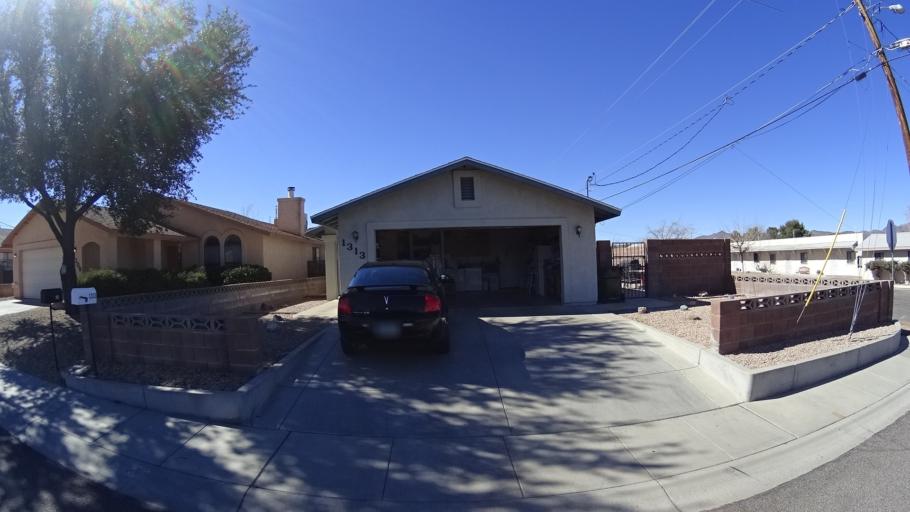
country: US
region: Arizona
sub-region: Mohave County
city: Kingman
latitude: 35.2008
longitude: -114.0314
